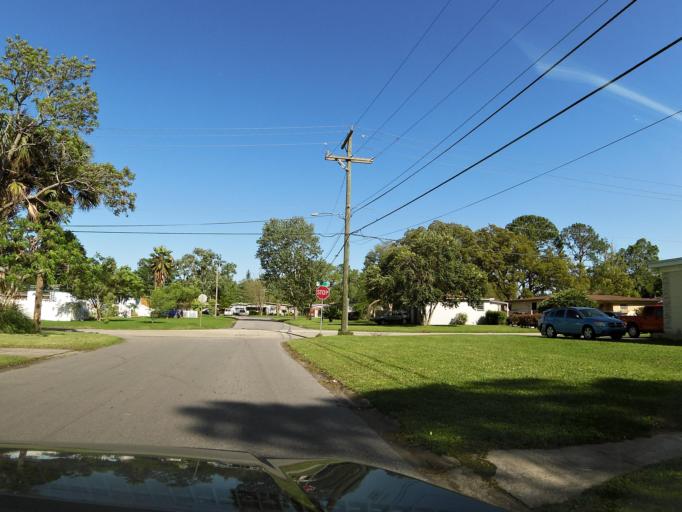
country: US
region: Florida
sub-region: Duval County
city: Jacksonville
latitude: 30.2834
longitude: -81.5961
